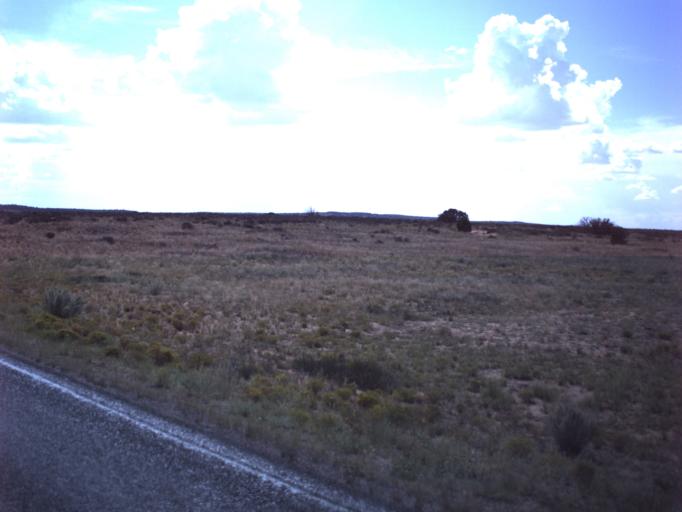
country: US
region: Utah
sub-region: Grand County
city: Moab
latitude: 38.6225
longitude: -109.8110
